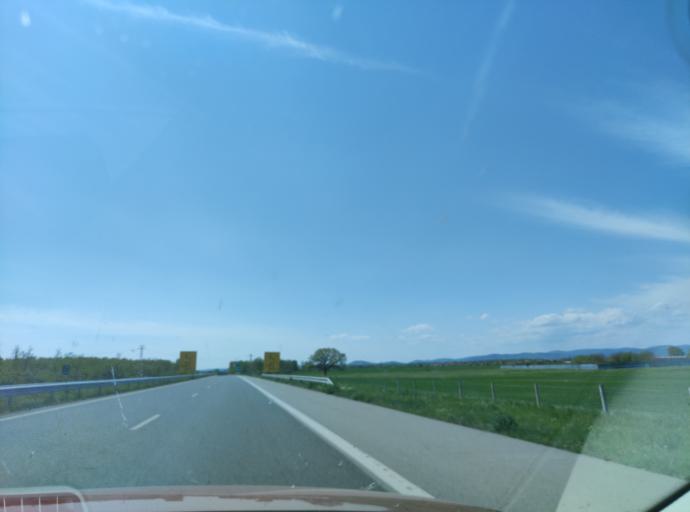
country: BG
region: Stara Zagora
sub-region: Obshtina Stara Zagora
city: Stara Zagora
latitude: 42.3433
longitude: 25.6847
